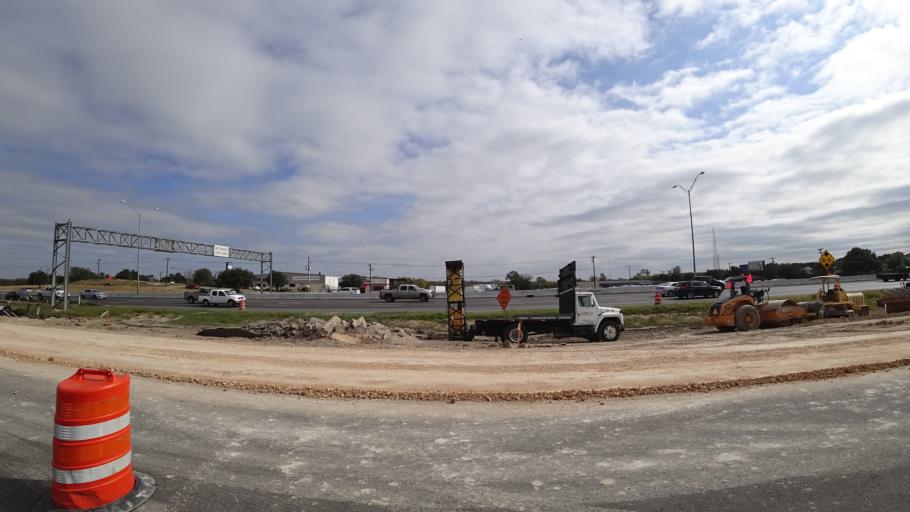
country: US
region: Texas
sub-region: Williamson County
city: Round Rock
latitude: 30.5448
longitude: -97.6928
